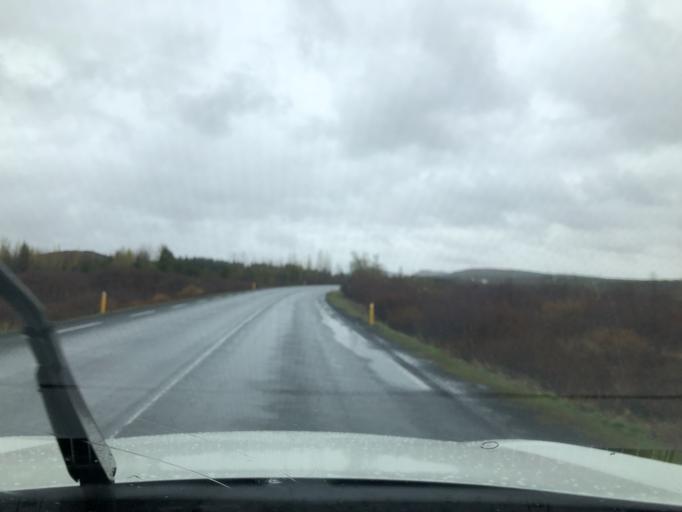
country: IS
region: South
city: Selfoss
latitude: 64.0215
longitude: -20.9306
